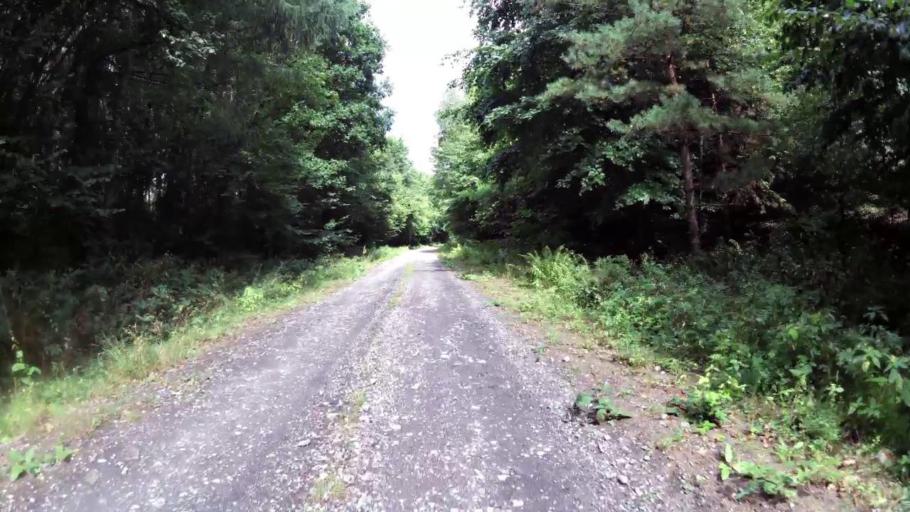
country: PL
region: West Pomeranian Voivodeship
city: Trzcinsko Zdroj
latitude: 52.8806
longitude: 14.6821
